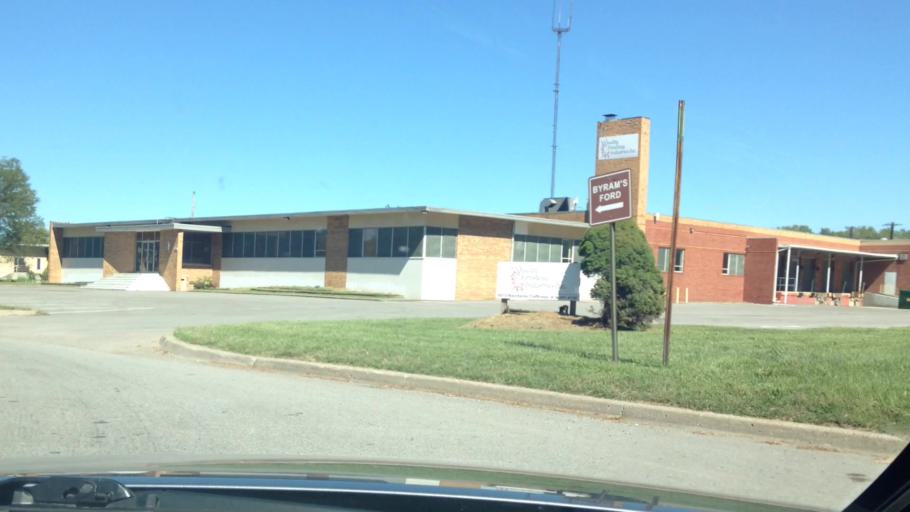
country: US
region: Missouri
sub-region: Jackson County
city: Raytown
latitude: 39.0155
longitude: -94.5261
